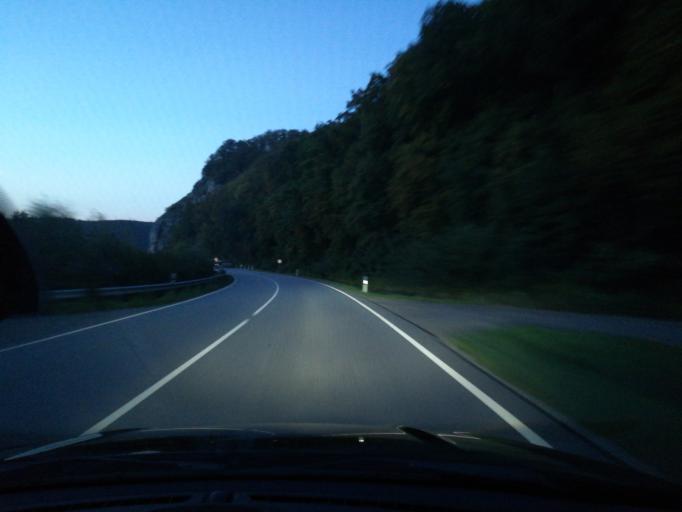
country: DE
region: Bavaria
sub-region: Lower Bavaria
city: Saal
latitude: 48.9091
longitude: 11.9724
